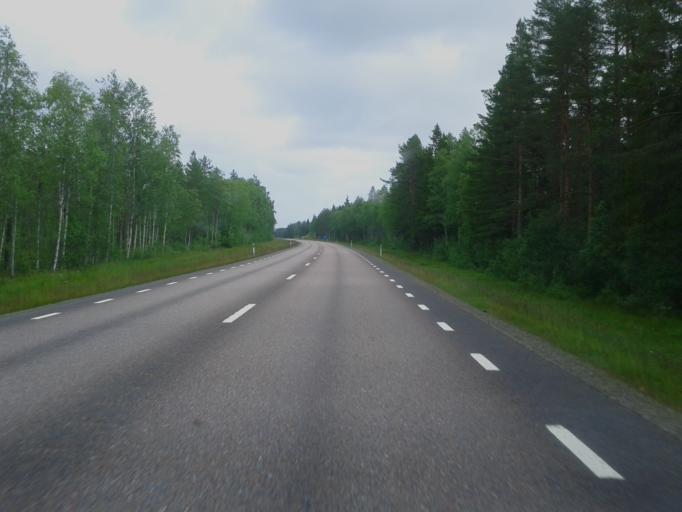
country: SE
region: Vaesterbotten
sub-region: Skelleftea Kommun
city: Burea
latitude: 64.3207
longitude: 21.1800
